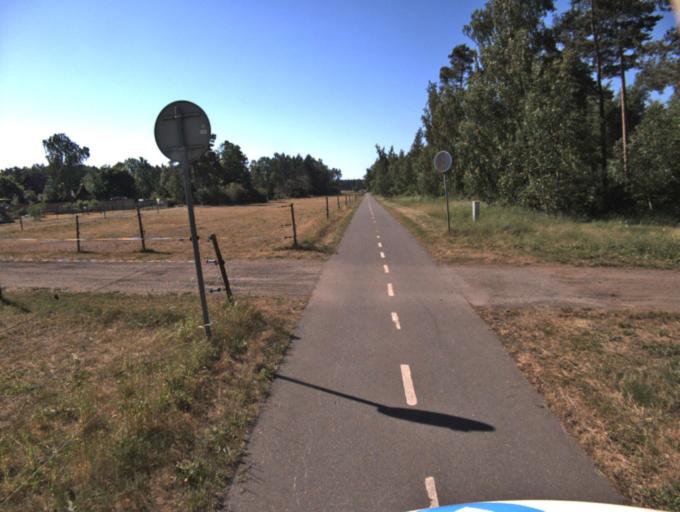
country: SE
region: Skane
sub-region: Kristianstads Kommun
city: Ahus
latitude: 55.9645
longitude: 14.2794
